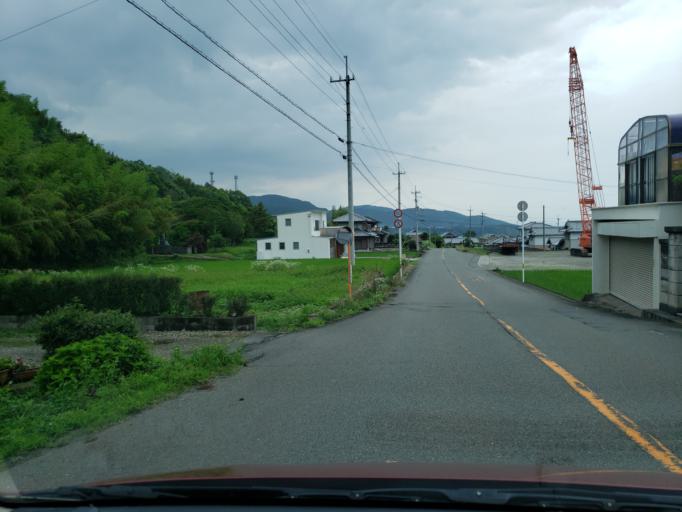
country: JP
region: Tokushima
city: Kamojimacho-jogejima
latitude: 34.1058
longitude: 134.2580
